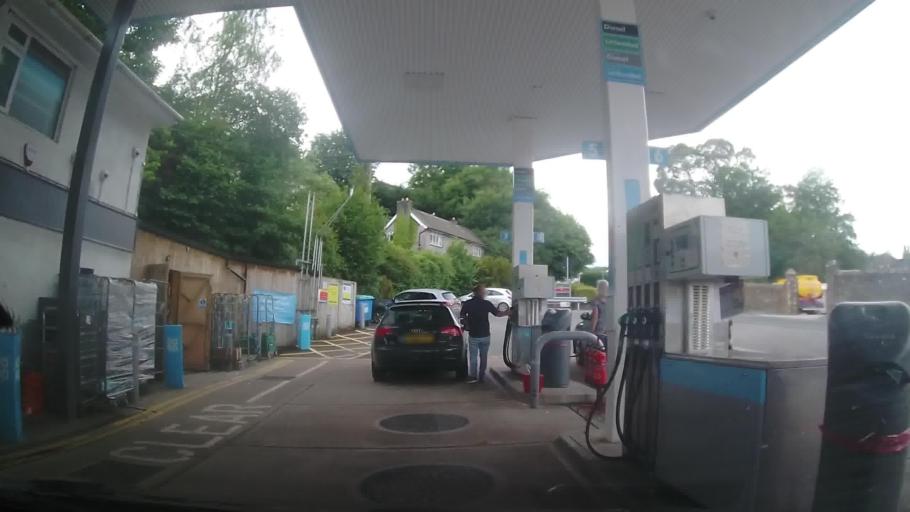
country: GB
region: England
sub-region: Devon
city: Kingsbridge
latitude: 50.2829
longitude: -3.7780
